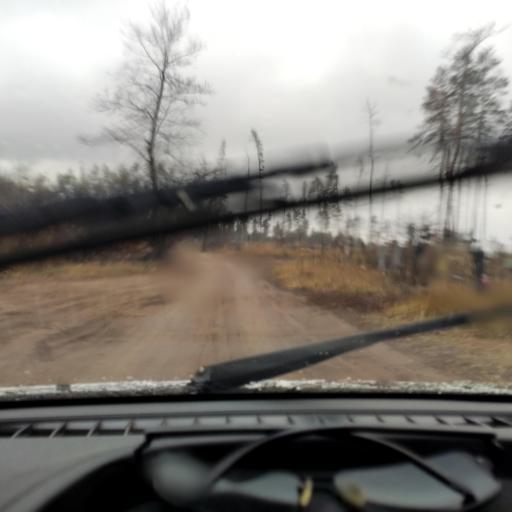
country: RU
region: Samara
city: Zhigulevsk
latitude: 53.5370
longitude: 49.5549
